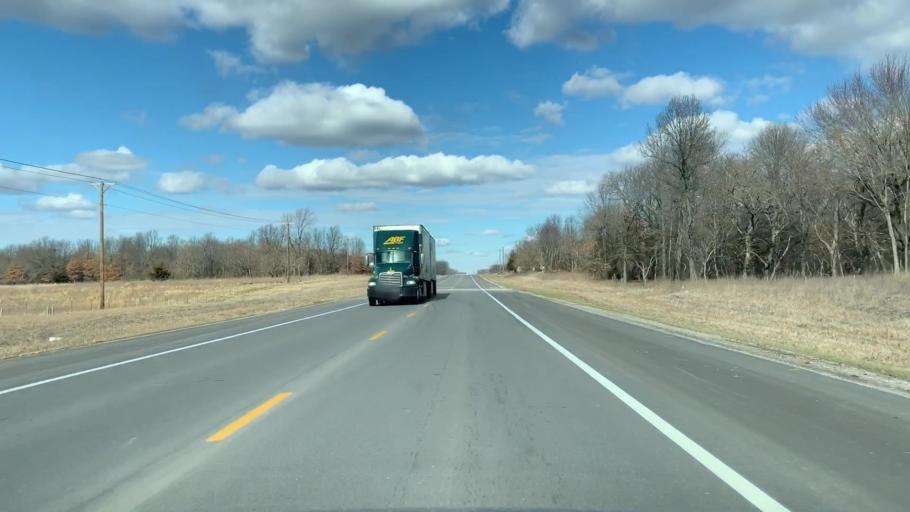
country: US
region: Kansas
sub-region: Cherokee County
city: Columbus
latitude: 37.2260
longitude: -94.8319
